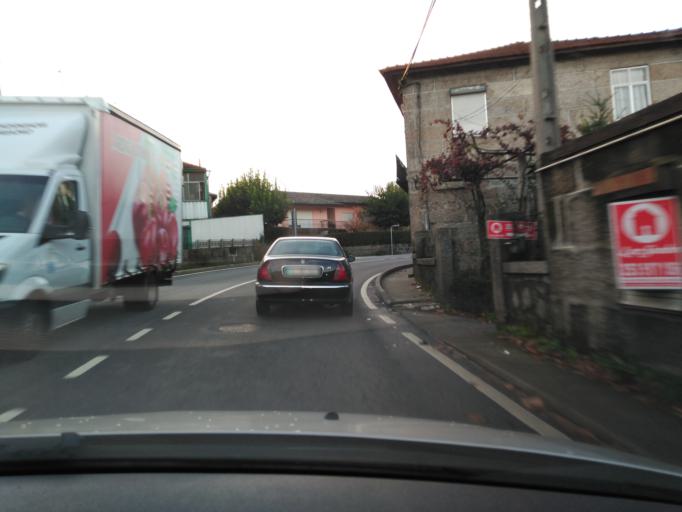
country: PT
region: Braga
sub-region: Guimaraes
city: Guimaraes
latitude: 41.4543
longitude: -8.3098
